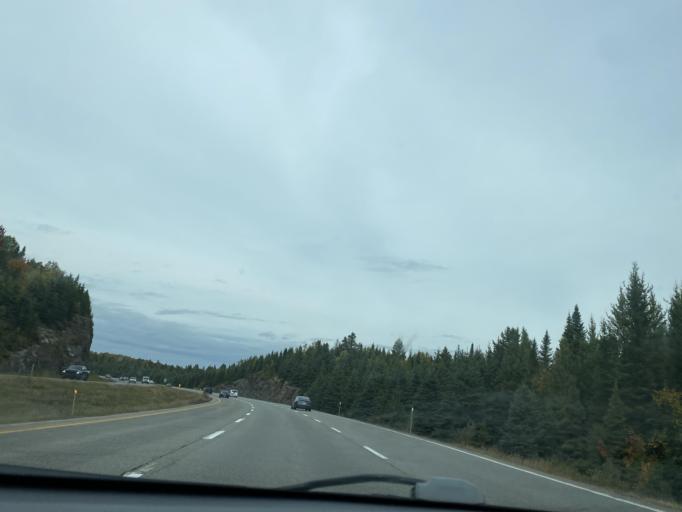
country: CA
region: Quebec
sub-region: Laurentides
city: Val-David
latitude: 46.0207
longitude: -74.2343
